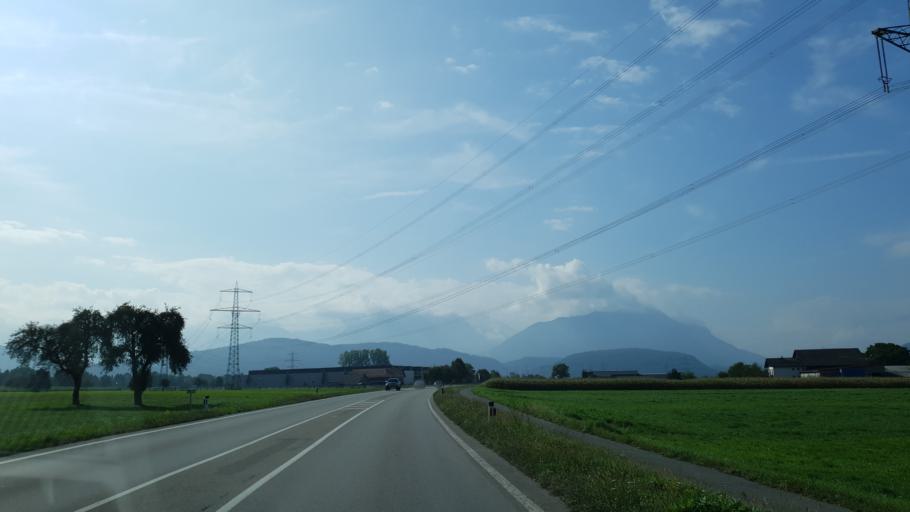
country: AT
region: Vorarlberg
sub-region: Politischer Bezirk Feldkirch
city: Weiler
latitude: 47.2940
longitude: 9.6211
